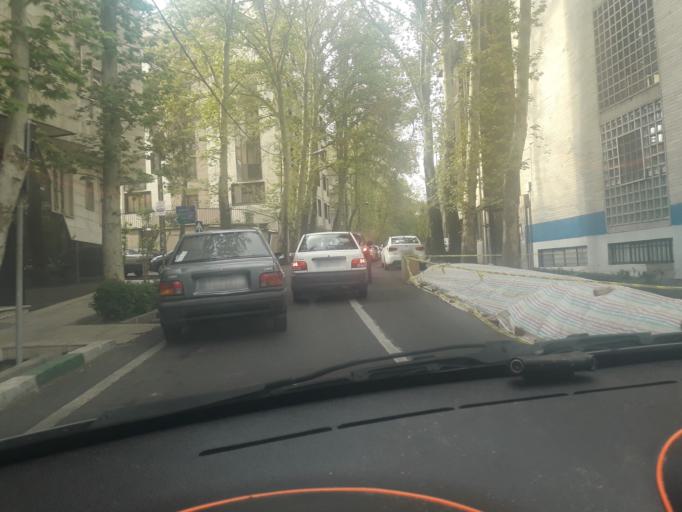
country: IR
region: Tehran
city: Tehran
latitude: 35.7399
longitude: 51.4064
